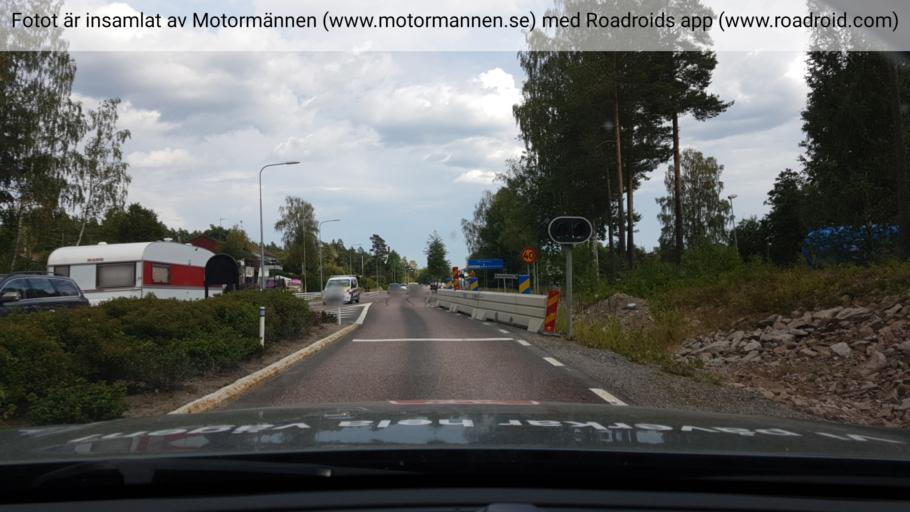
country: SE
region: Uppsala
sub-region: Enkopings Kommun
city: Orsundsbro
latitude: 59.8875
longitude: 17.1911
